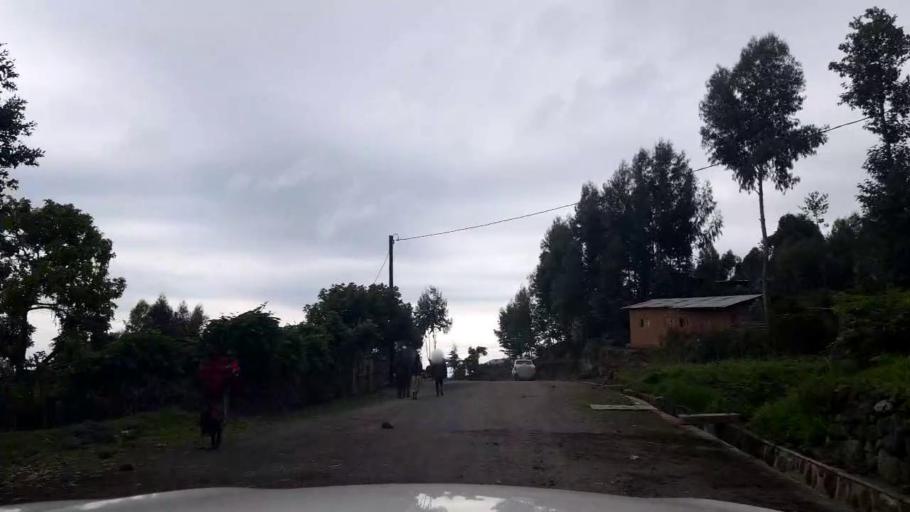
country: RW
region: Northern Province
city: Musanze
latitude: -1.4888
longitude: 29.5293
